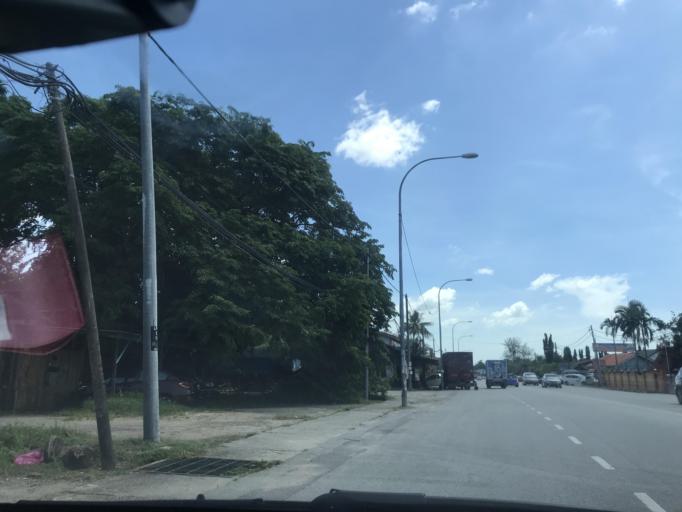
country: MY
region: Kelantan
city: Kota Bharu
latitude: 6.1069
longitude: 102.2631
